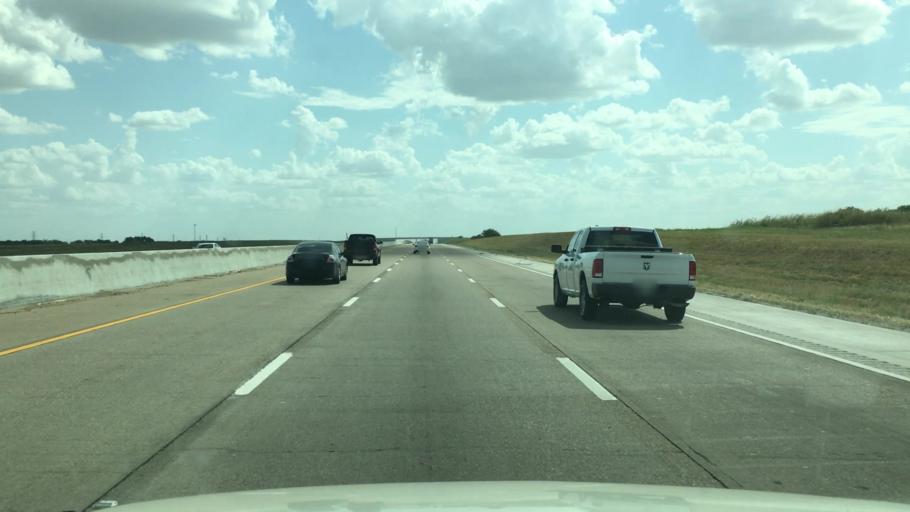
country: US
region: Texas
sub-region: Ellis County
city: Italy
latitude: 32.1566
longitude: -96.9268
